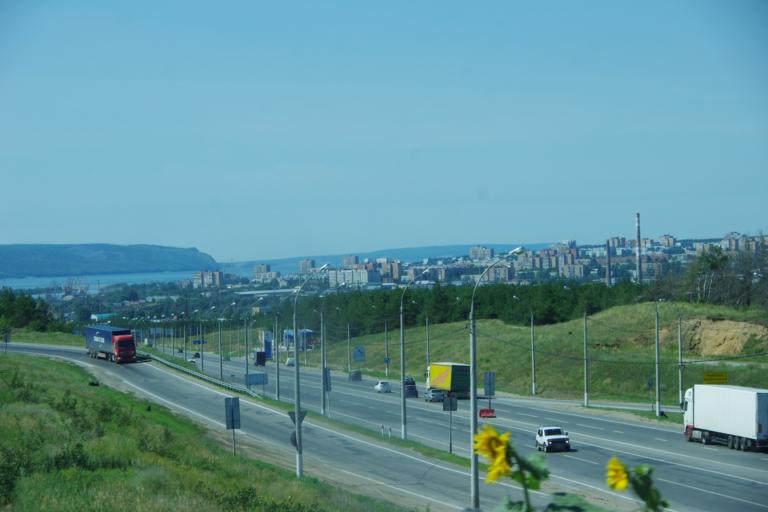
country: RU
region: Samara
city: Zhigulevsk
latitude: 53.4988
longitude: 49.5408
